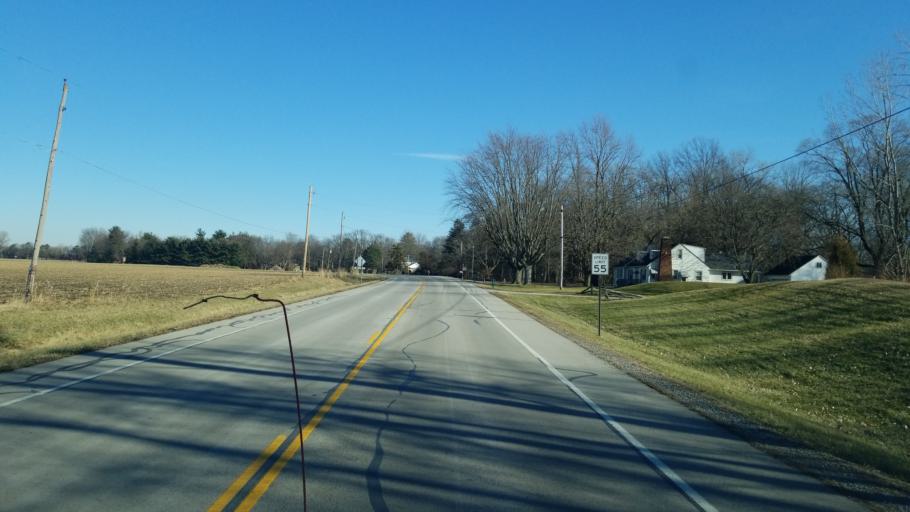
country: US
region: Ohio
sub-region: Lucas County
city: Waterville
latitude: 41.4671
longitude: -83.7654
